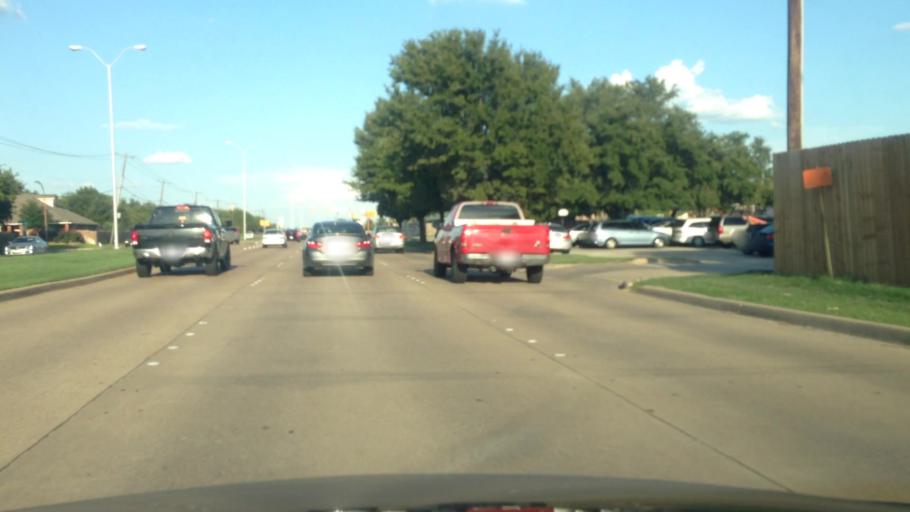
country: US
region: Texas
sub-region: Tarrant County
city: Watauga
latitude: 32.8609
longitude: -97.2828
